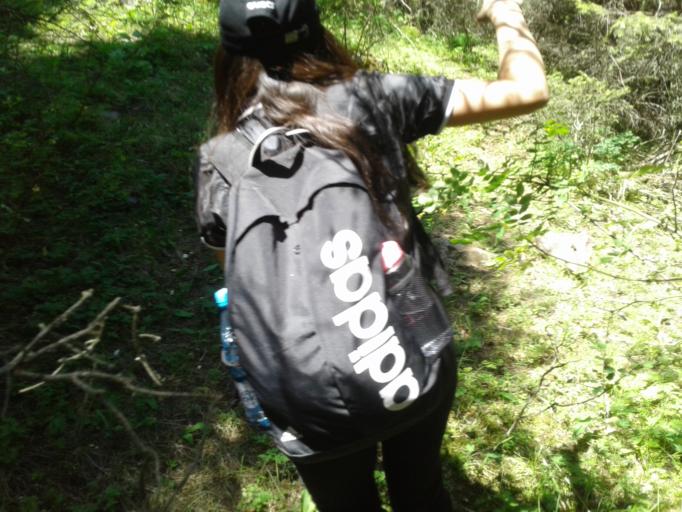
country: KG
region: Naryn
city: Naryn
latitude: 41.4187
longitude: 76.1859
